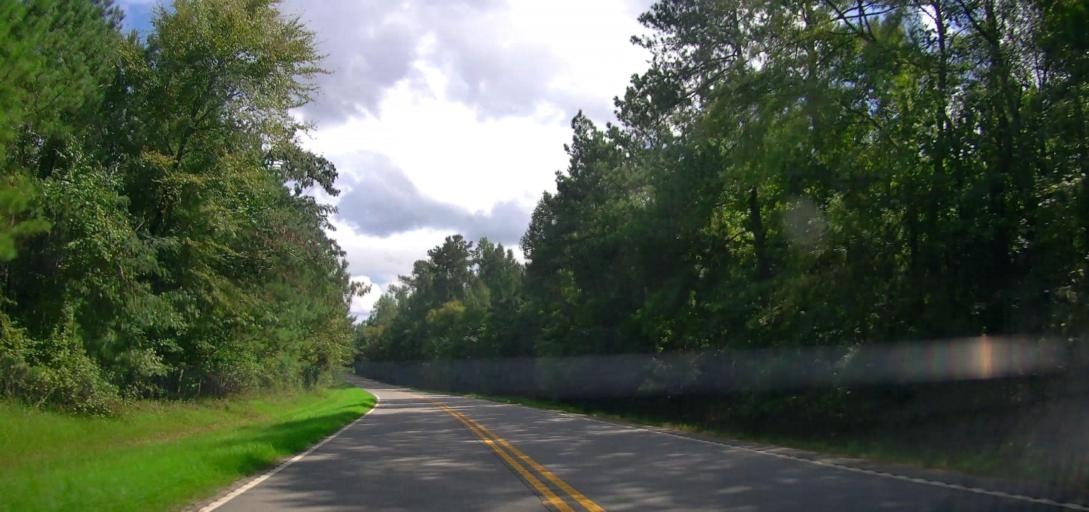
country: US
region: Georgia
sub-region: Talbot County
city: Talbotton
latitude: 32.6472
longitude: -84.5050
